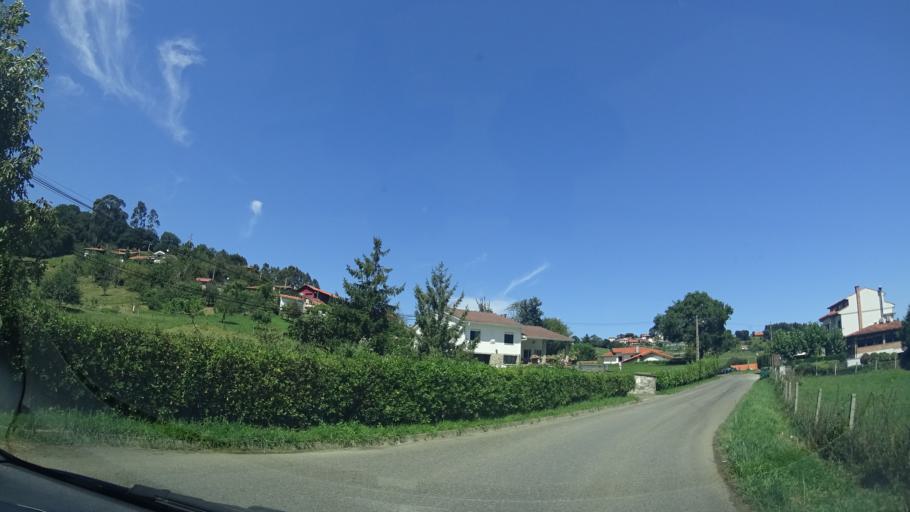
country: ES
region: Asturias
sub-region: Province of Asturias
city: Ribadesella
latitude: 43.4524
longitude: -5.0737
